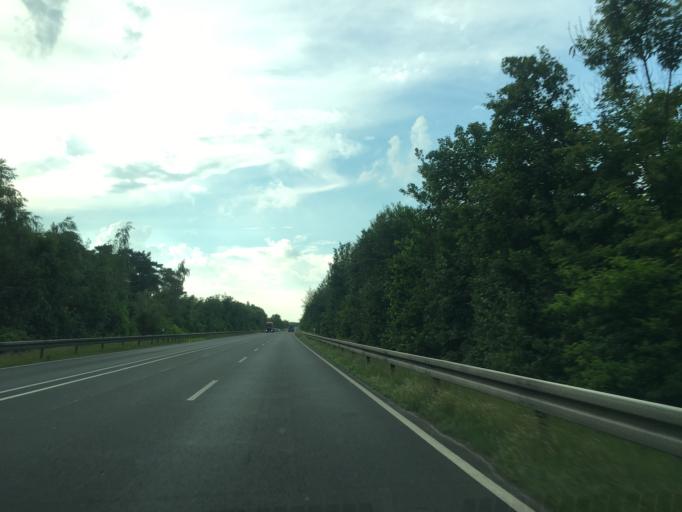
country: DE
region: North Rhine-Westphalia
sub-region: Regierungsbezirk Munster
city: Metelen
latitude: 52.1744
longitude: 7.2545
